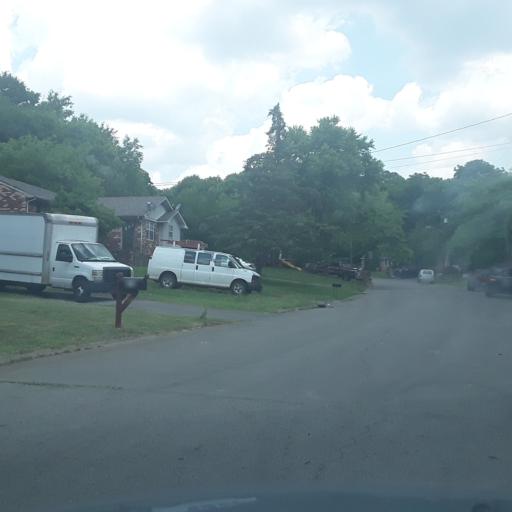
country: US
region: Tennessee
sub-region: Williamson County
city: Brentwood Estates
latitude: 36.0525
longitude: -86.7013
